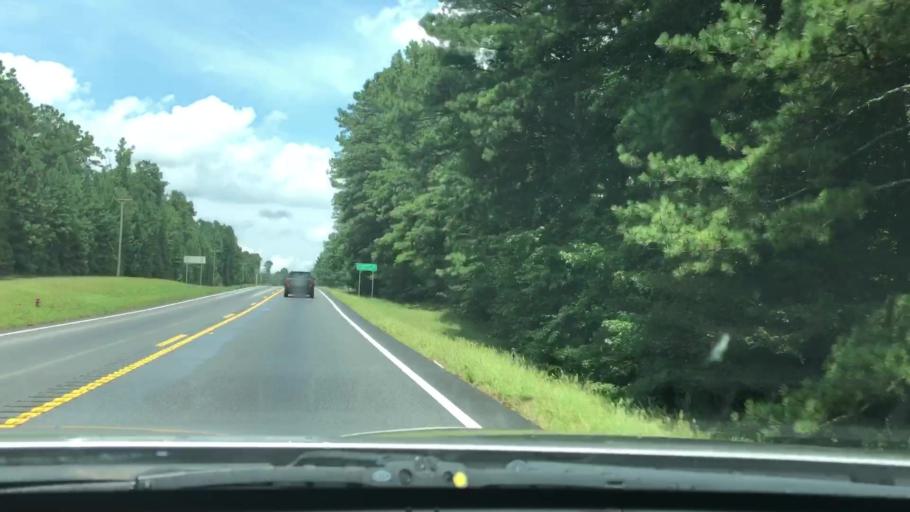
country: US
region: Georgia
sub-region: Lamar County
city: Barnesville
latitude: 33.1066
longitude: -84.1546
